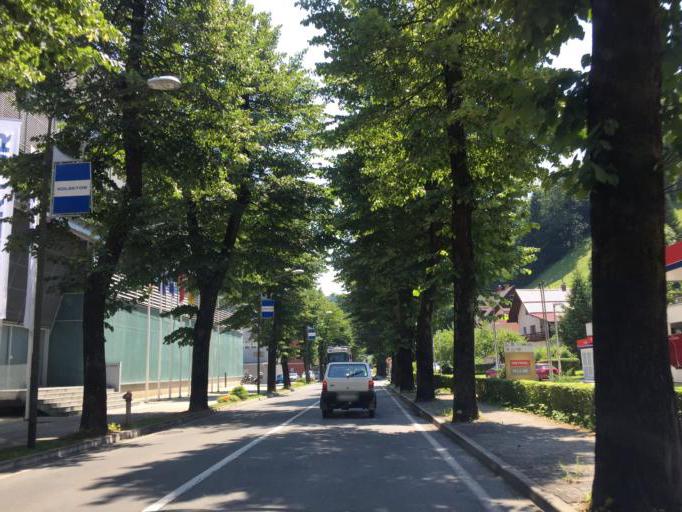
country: SI
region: Idrija
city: Idrija
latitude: 46.0065
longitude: 14.0278
